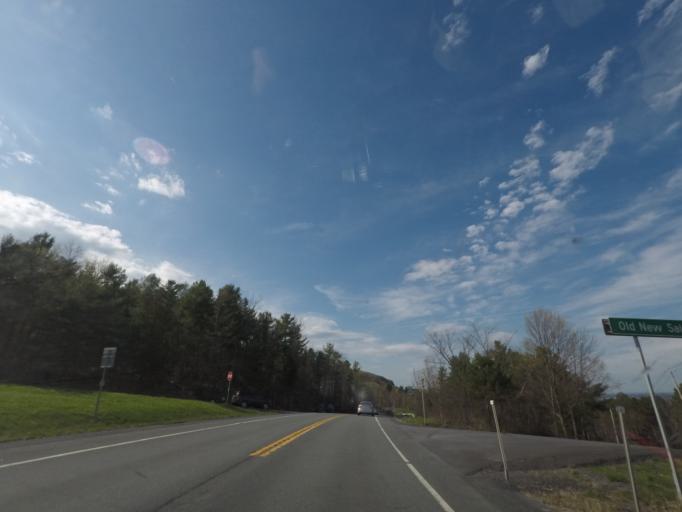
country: US
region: New York
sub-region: Albany County
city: Voorheesville
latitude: 42.6155
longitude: -73.9750
